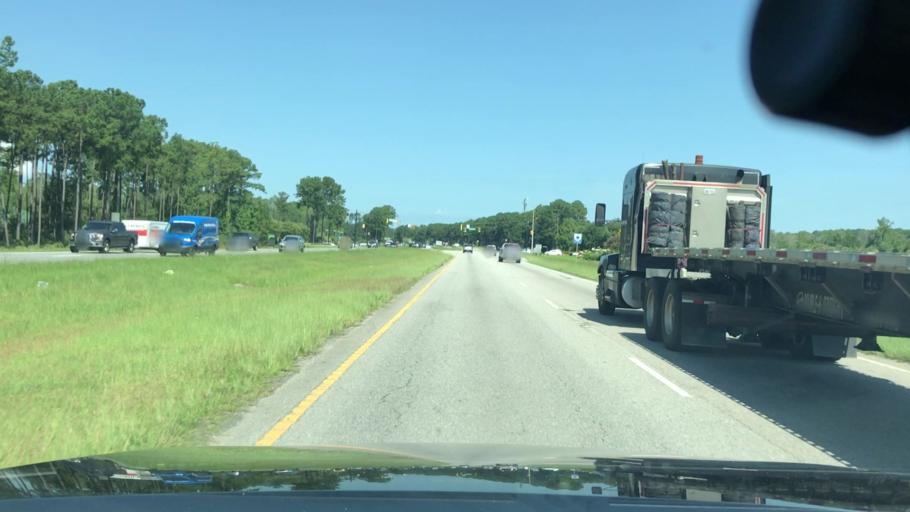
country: US
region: South Carolina
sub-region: Jasper County
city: Hardeeville
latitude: 32.3067
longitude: -80.9742
